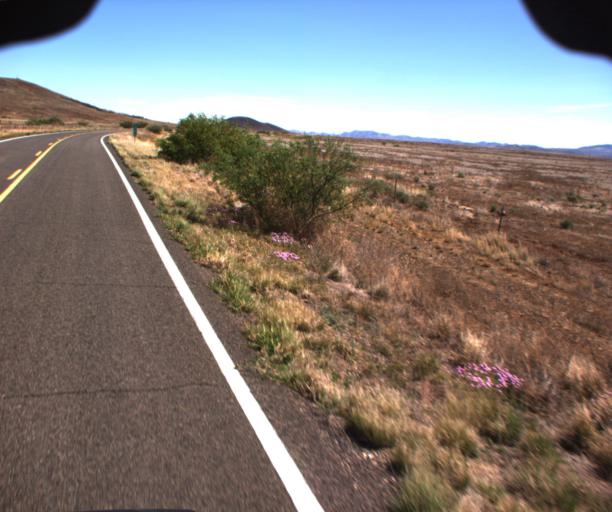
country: US
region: Arizona
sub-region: Cochise County
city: Douglas
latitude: 31.5451
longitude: -109.2831
